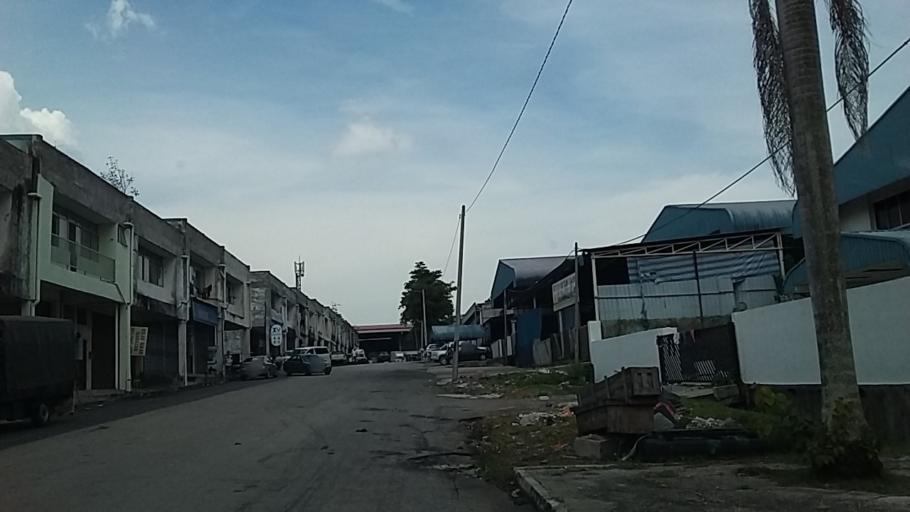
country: MY
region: Johor
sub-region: Daerah Batu Pahat
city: Batu Pahat
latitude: 1.7869
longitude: 102.9681
